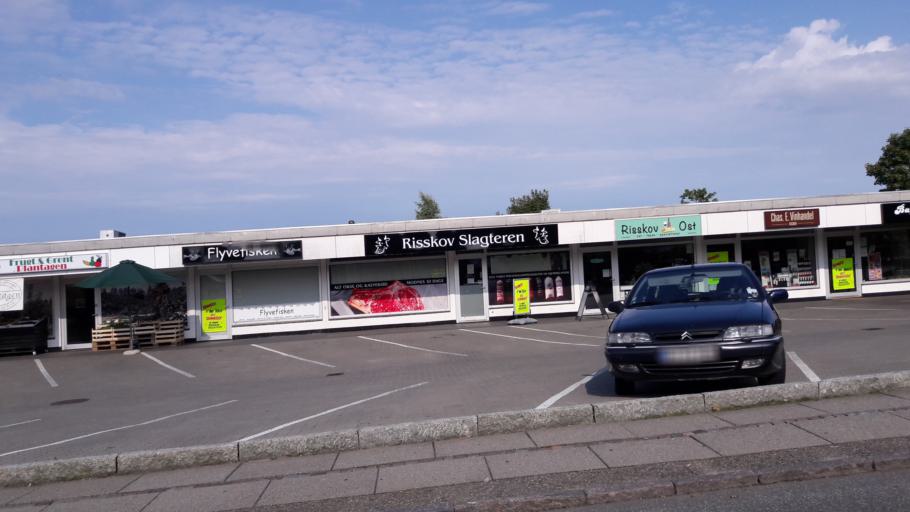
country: DK
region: Central Jutland
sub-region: Arhus Kommune
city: Lystrup
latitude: 56.1942
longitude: 10.2339
